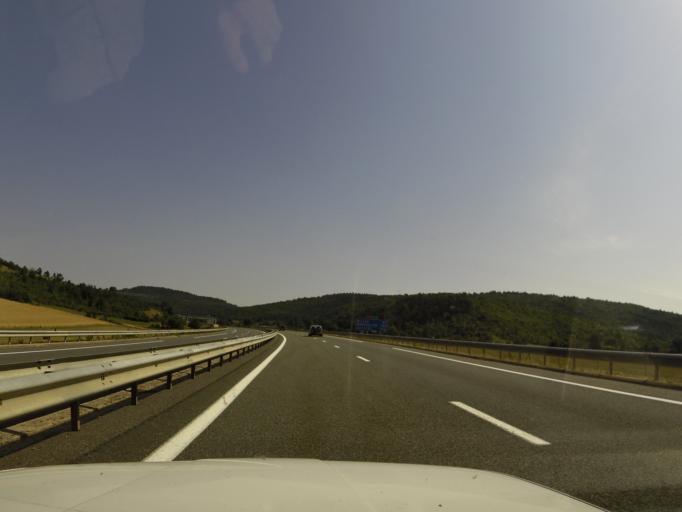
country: FR
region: Midi-Pyrenees
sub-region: Departement de l'Aveyron
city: Severac-le-Chateau
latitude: 44.3749
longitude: 3.1146
